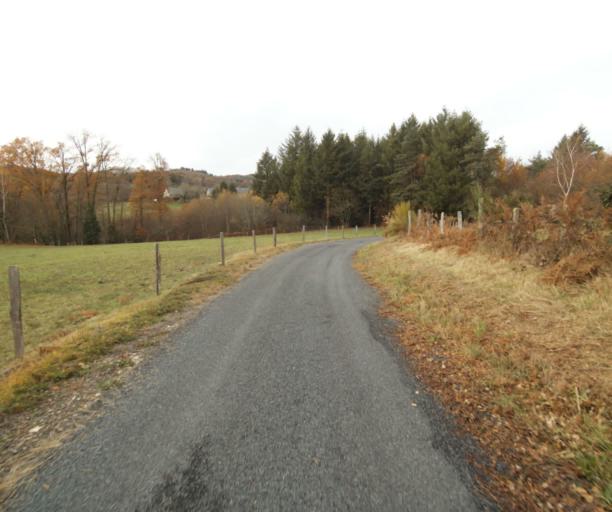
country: FR
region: Limousin
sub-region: Departement de la Correze
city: Sainte-Fortunade
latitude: 45.1791
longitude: 1.7857
